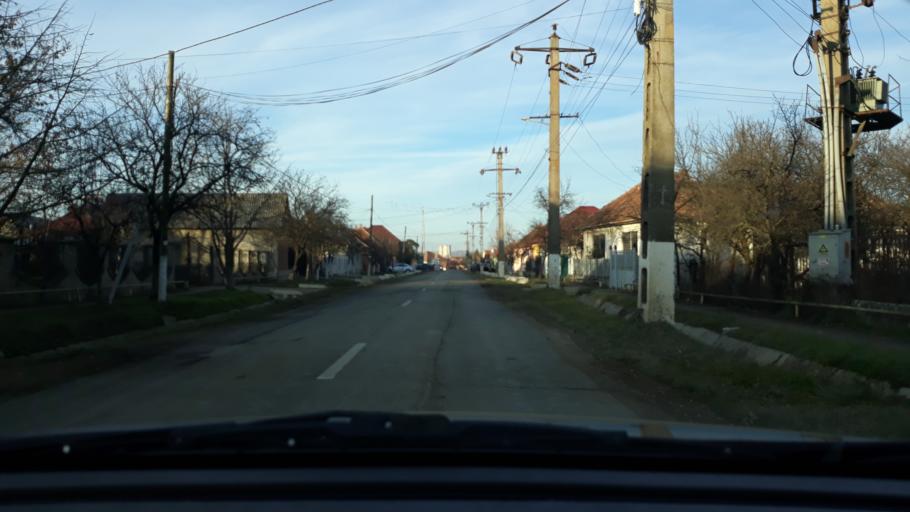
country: RO
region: Bihor
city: Foglas
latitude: 47.2500
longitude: 22.5330
